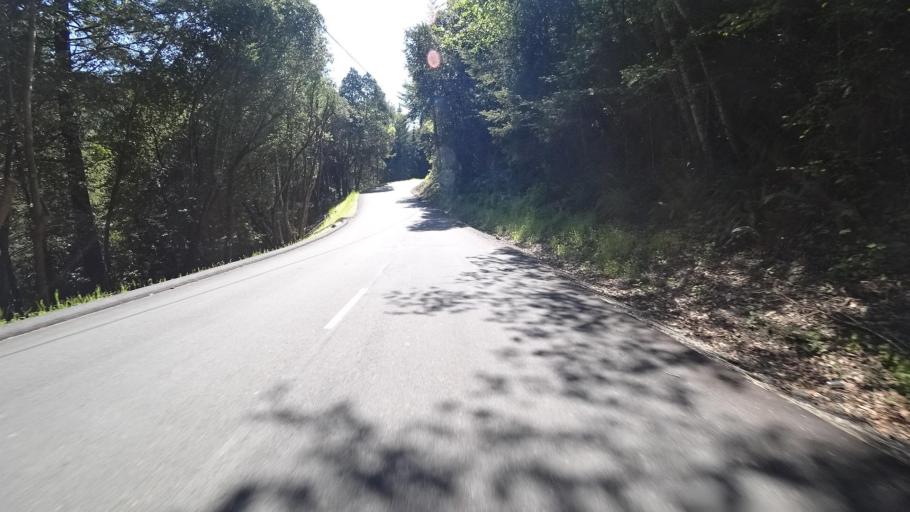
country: US
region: California
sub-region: Humboldt County
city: Rio Dell
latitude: 40.2704
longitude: -124.2063
